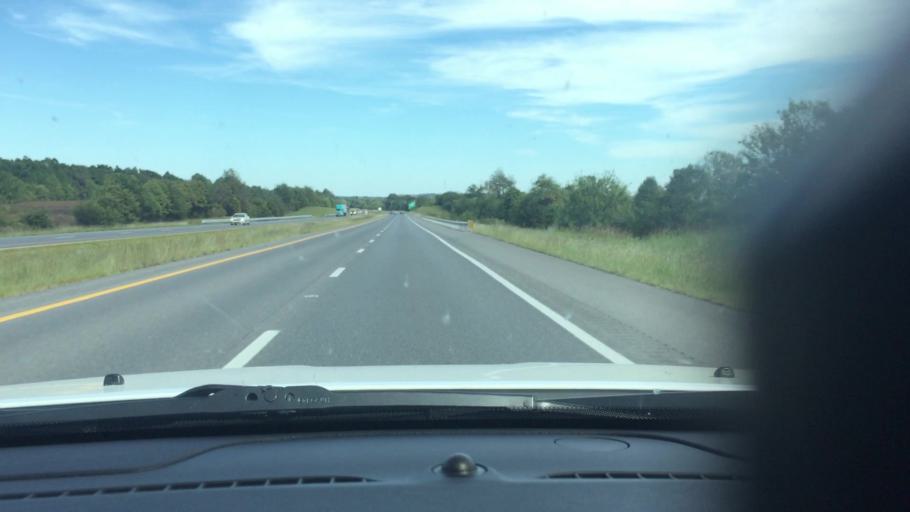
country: US
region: Kentucky
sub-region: Caldwell County
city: Princeton
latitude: 37.1118
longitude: -87.9409
